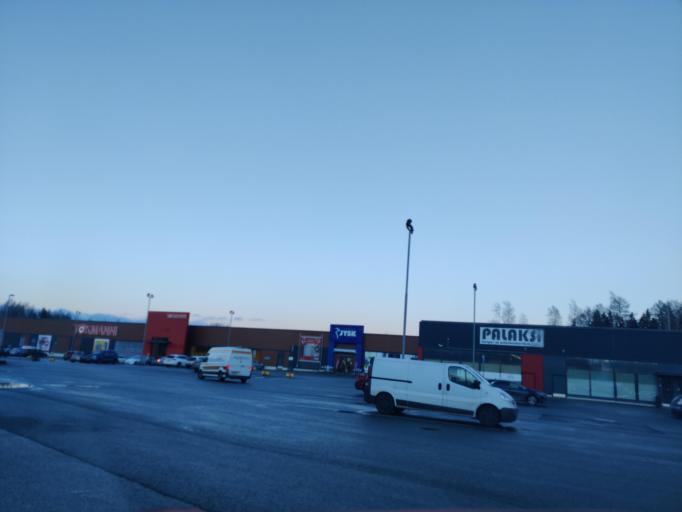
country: FI
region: Pirkanmaa
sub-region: Tampere
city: Nokia
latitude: 61.4667
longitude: 23.5123
